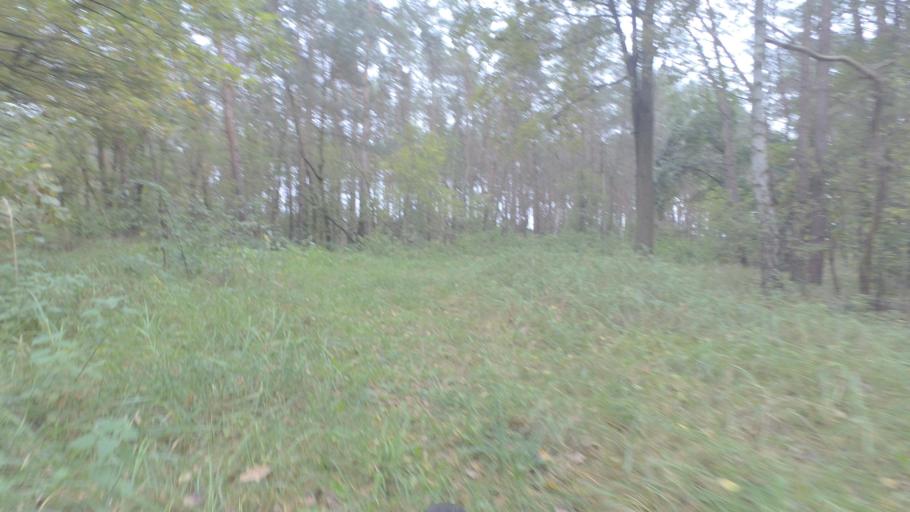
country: DE
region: Brandenburg
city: Rangsdorf
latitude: 52.2800
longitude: 13.3503
